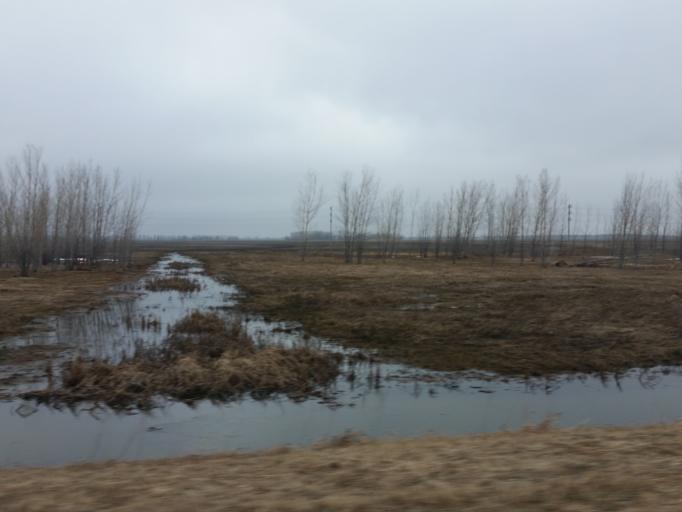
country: US
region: North Dakota
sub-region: Walsh County
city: Grafton
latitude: 48.3532
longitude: -97.1801
